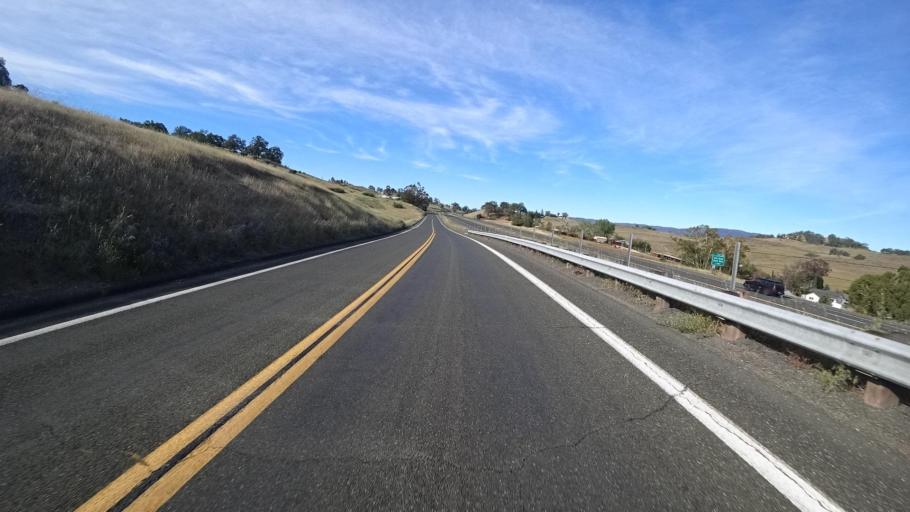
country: US
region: California
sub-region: Lake County
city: North Lakeport
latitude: 39.0994
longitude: -122.9131
